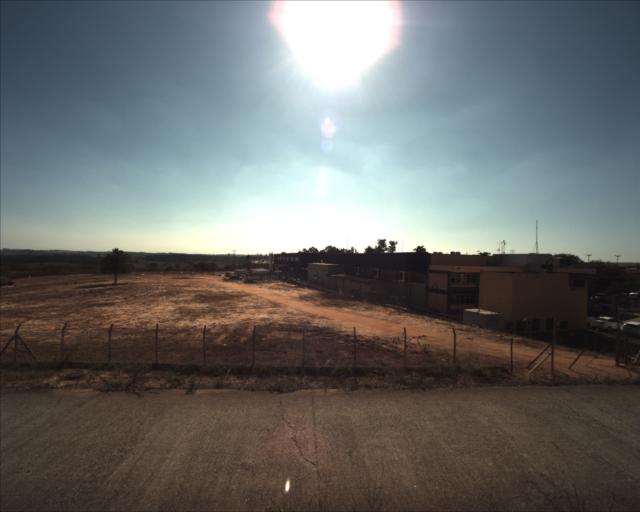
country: BR
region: Sao Paulo
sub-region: Sorocaba
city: Sorocaba
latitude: -23.4070
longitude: -47.3832
